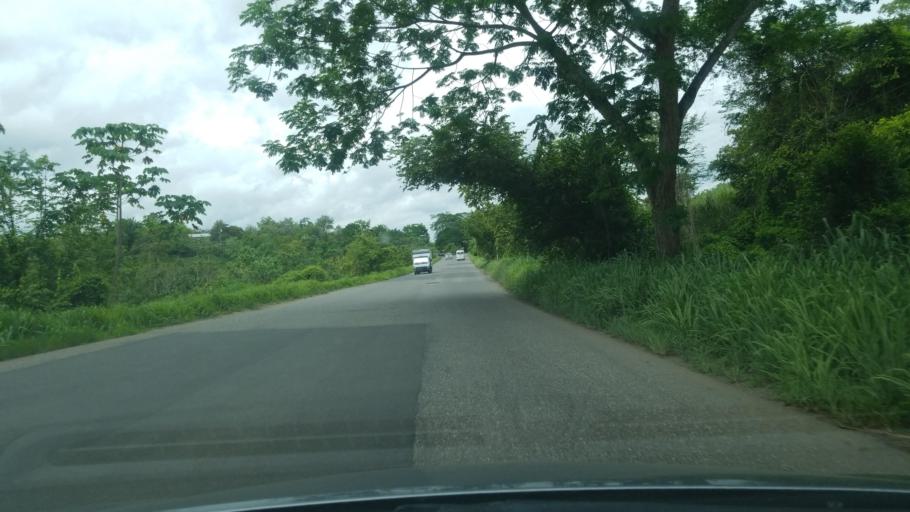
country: HN
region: Santa Barbara
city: La Flecha
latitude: 15.3010
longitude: -88.4554
